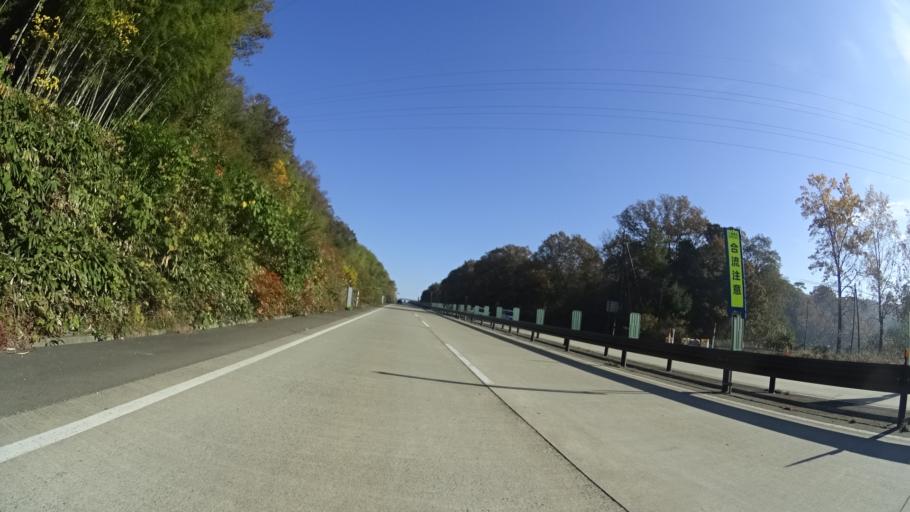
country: JP
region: Ishikawa
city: Komatsu
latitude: 36.3789
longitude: 136.4813
